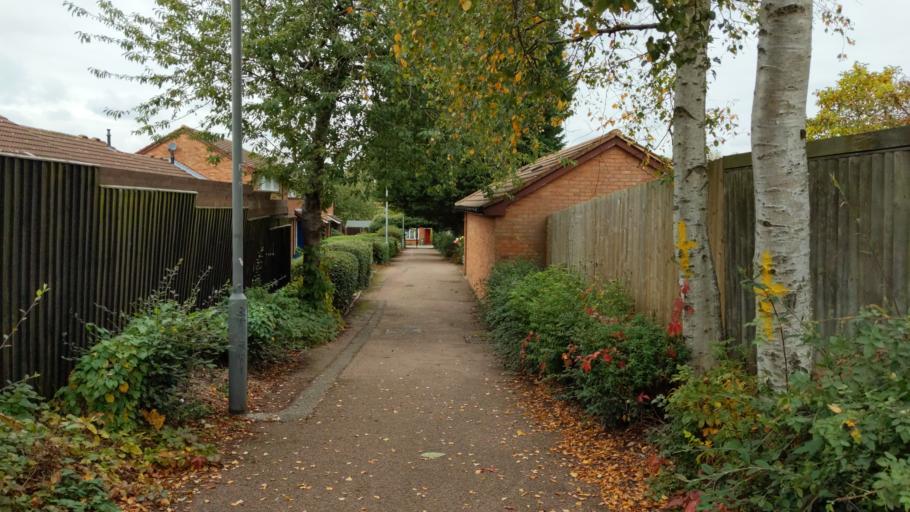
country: GB
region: England
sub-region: Buckinghamshire
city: Bletchley
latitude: 52.0098
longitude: -0.7584
